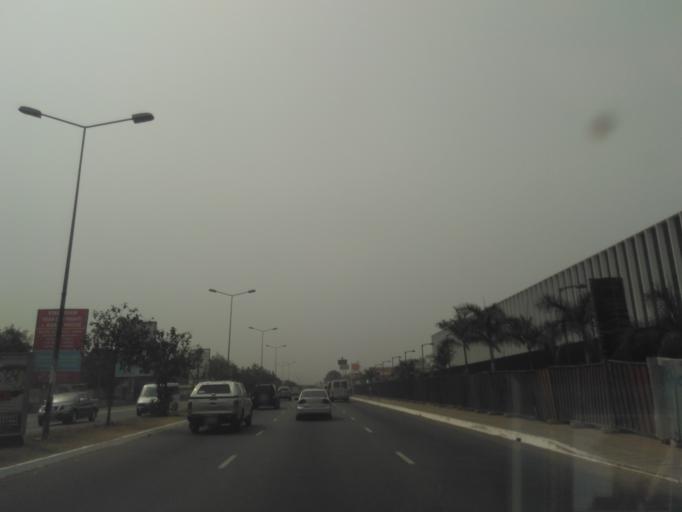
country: GH
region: Greater Accra
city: Accra
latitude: 5.5956
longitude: -0.1800
